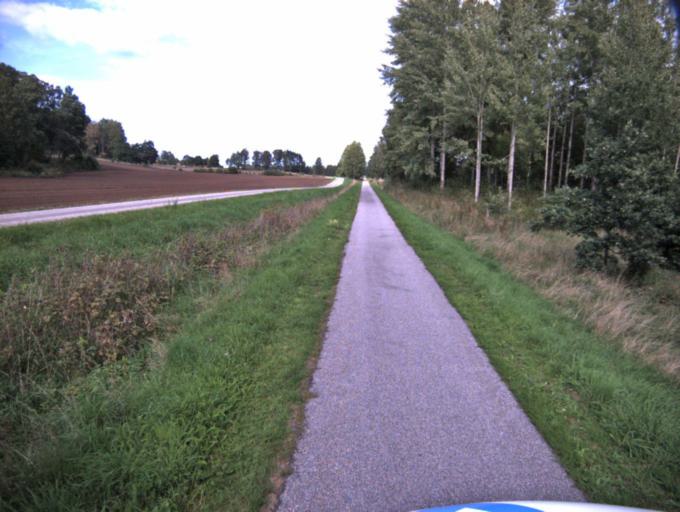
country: SE
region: Vaestra Goetaland
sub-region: Ulricehamns Kommun
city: Ulricehamn
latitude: 57.8460
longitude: 13.4229
